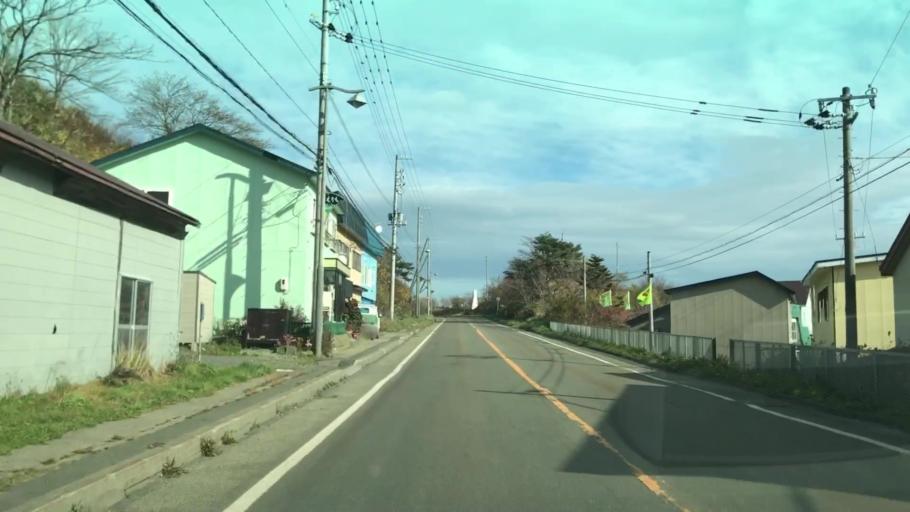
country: JP
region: Hokkaido
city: Obihiro
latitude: 42.0443
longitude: 143.2964
